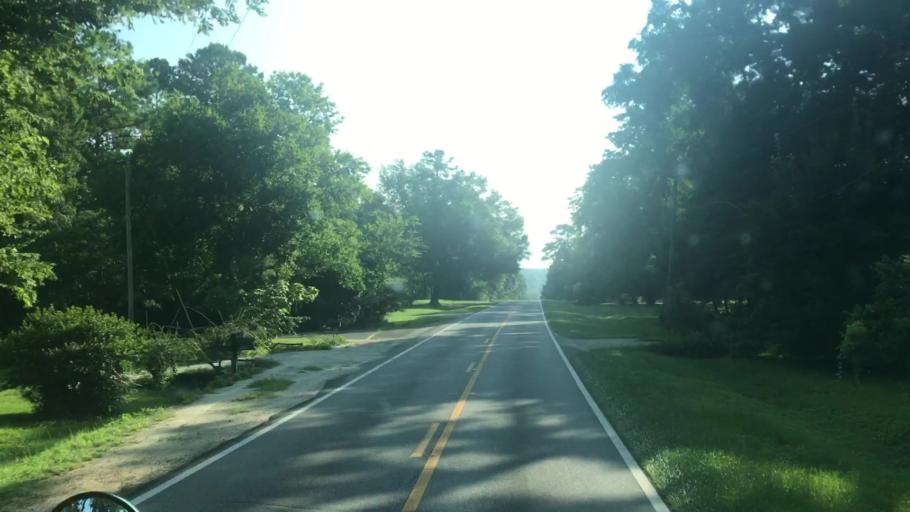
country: US
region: Florida
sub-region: Gadsden County
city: Quincy
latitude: 30.6620
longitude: -84.5594
